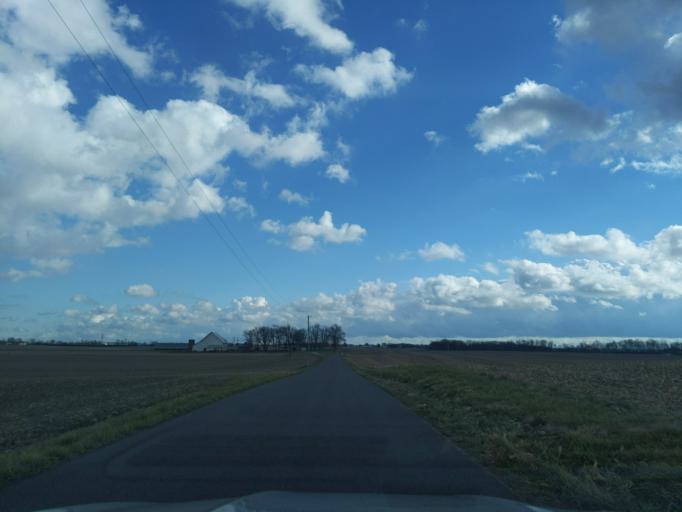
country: US
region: Indiana
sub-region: Decatur County
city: Greensburg
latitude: 39.3803
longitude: -85.5067
